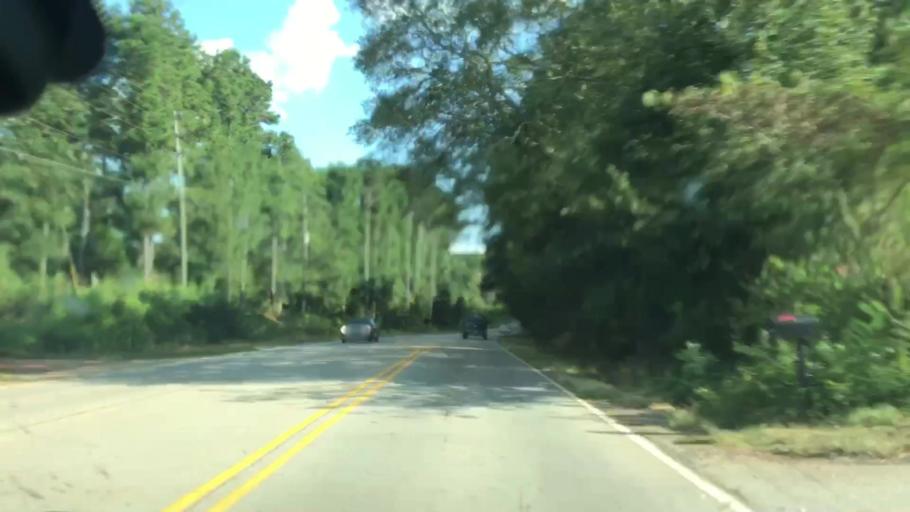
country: US
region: Georgia
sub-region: Troup County
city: La Grange
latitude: 32.9708
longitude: -84.9864
